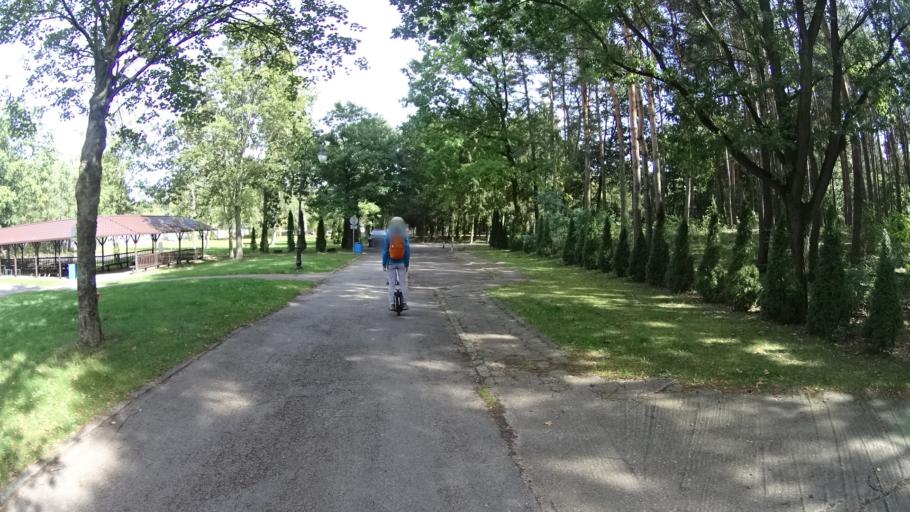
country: PL
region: Masovian Voivodeship
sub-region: Powiat legionowski
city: Bialobrzegi
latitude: 52.4610
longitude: 21.0704
